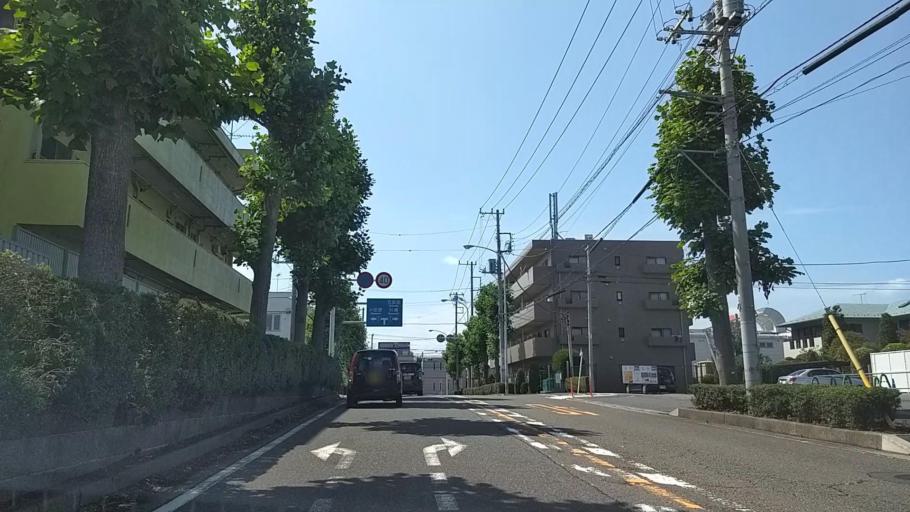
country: JP
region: Kanagawa
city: Fujisawa
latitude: 35.3683
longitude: 139.5013
